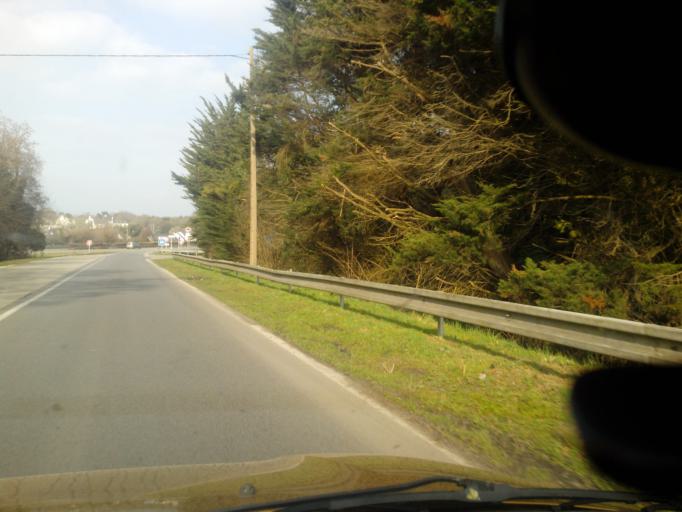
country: FR
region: Brittany
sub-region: Departement du Morbihan
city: Vannes
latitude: 47.6704
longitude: -2.7215
